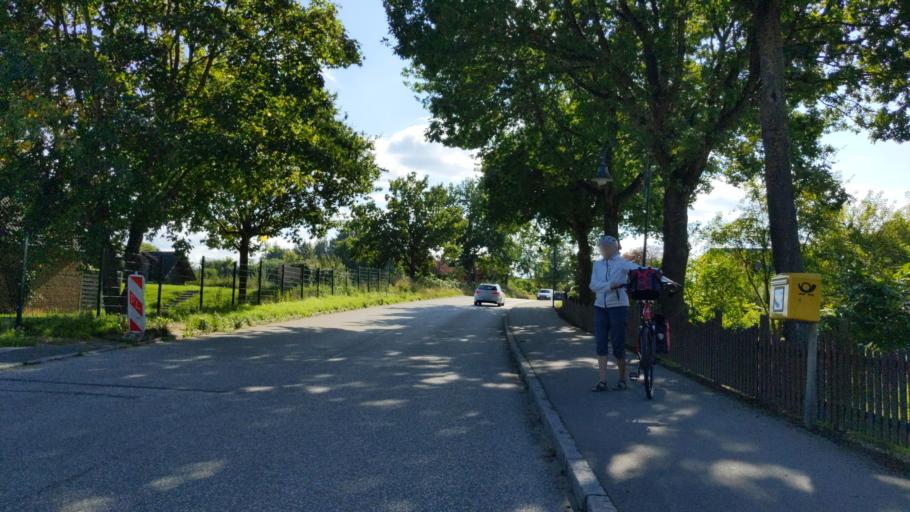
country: DE
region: Schleswig-Holstein
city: Schonwalde am Bungsberg
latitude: 54.1823
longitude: 10.7487
